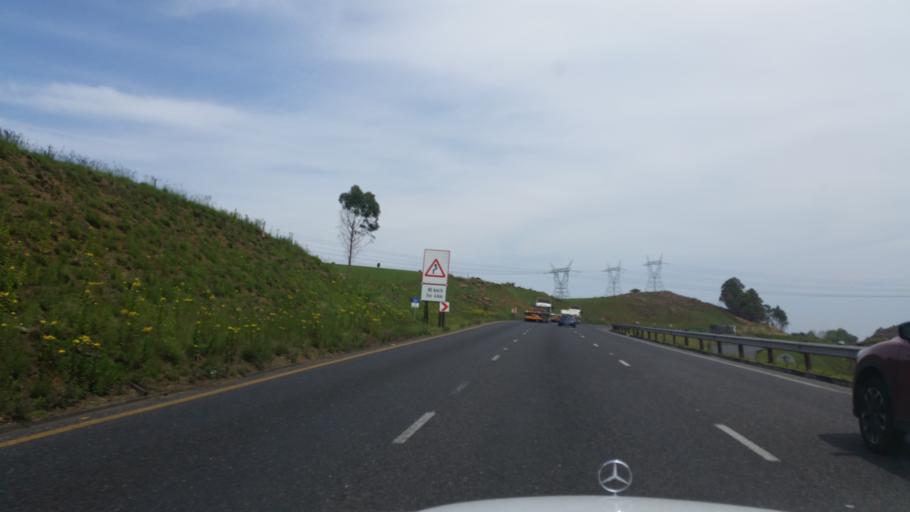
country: ZA
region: KwaZulu-Natal
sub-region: uMgungundlovu District Municipality
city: Howick
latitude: -29.4396
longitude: 30.1745
